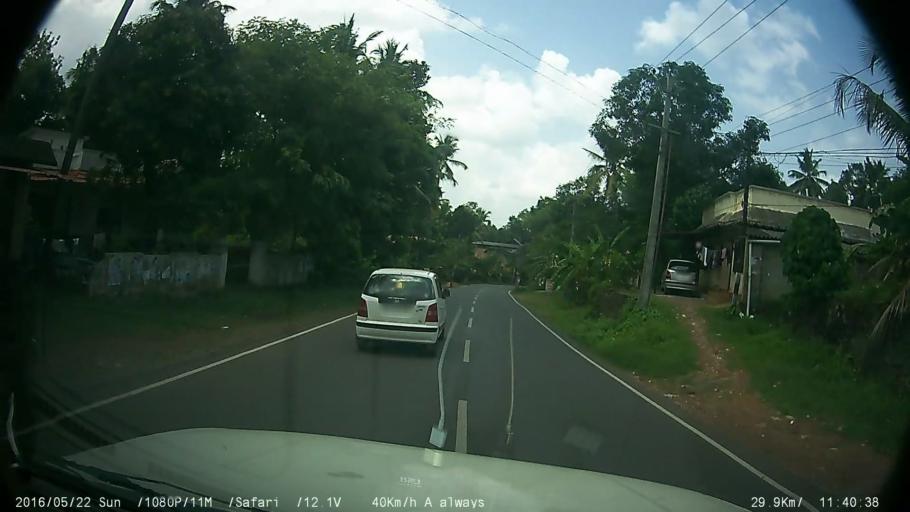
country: IN
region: Kerala
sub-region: Kottayam
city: Kottayam
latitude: 9.5538
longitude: 76.5178
